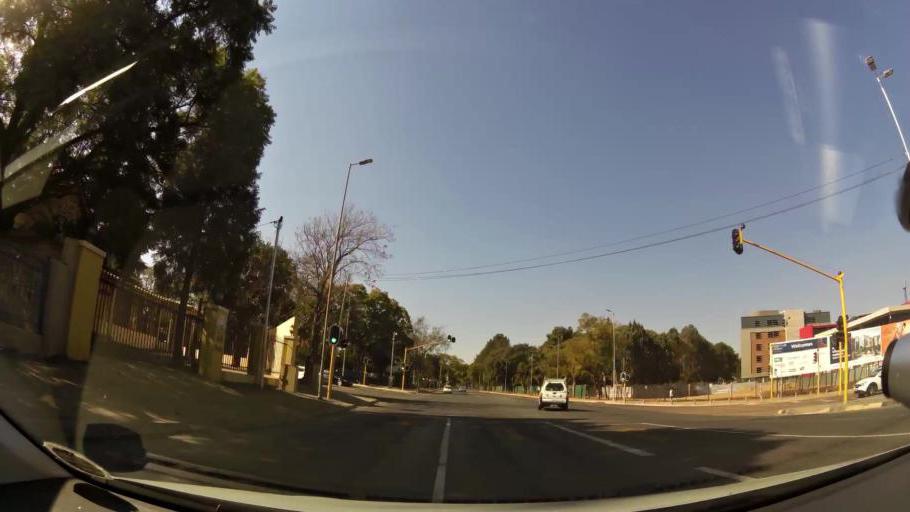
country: ZA
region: Gauteng
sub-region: City of Tshwane Metropolitan Municipality
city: Pretoria
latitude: -25.7500
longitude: 28.2222
